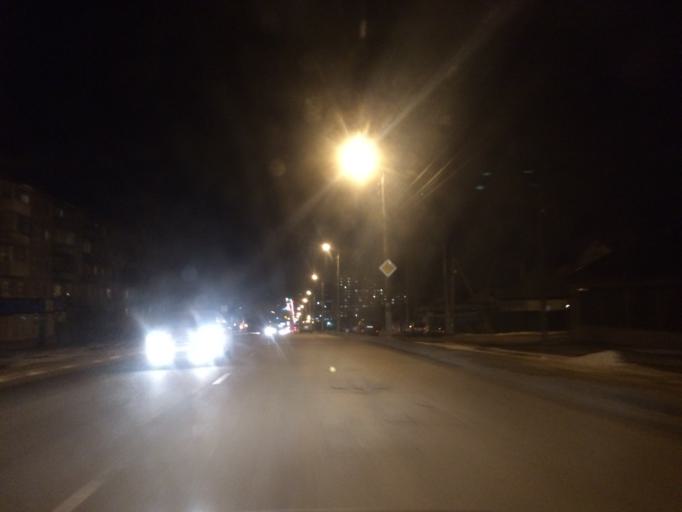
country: RU
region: Tula
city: Tula
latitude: 54.1987
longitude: 37.6860
